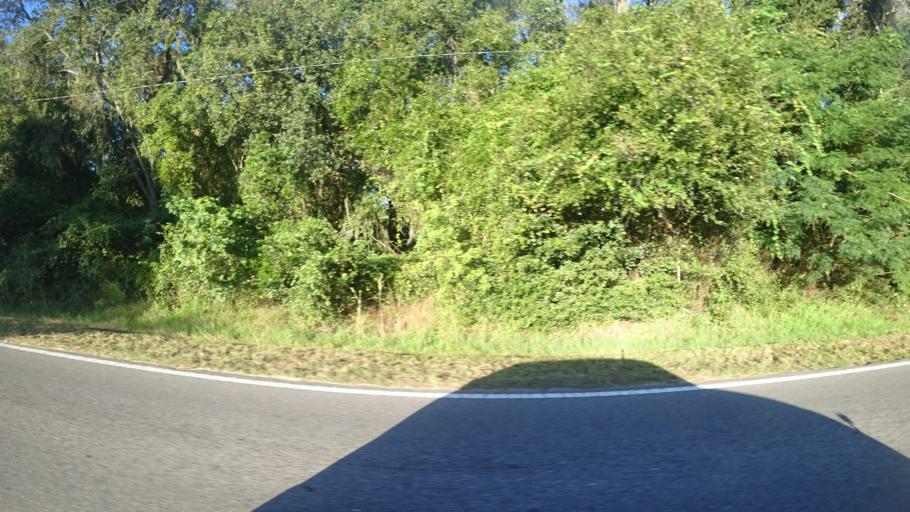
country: US
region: Florida
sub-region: Manatee County
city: Ellenton
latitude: 27.5459
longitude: -82.5283
